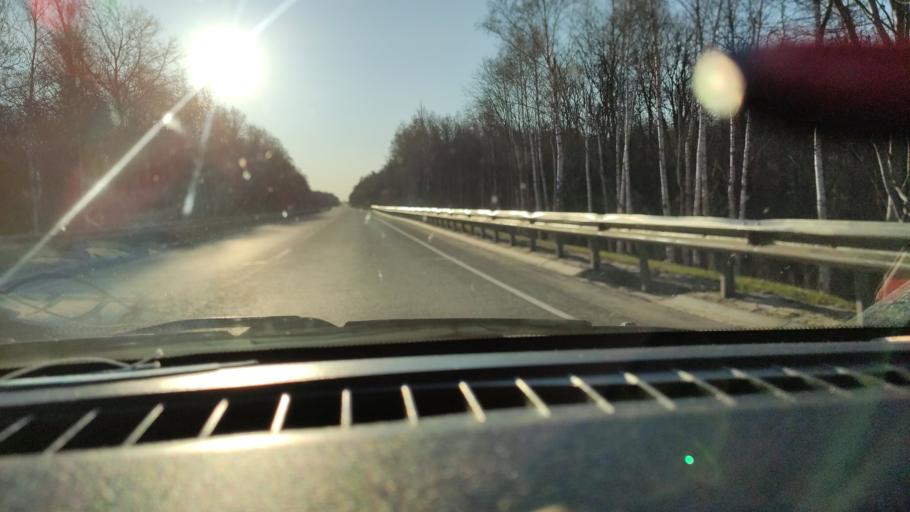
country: RU
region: Saratov
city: Vol'sk
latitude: 52.1117
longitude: 47.3348
